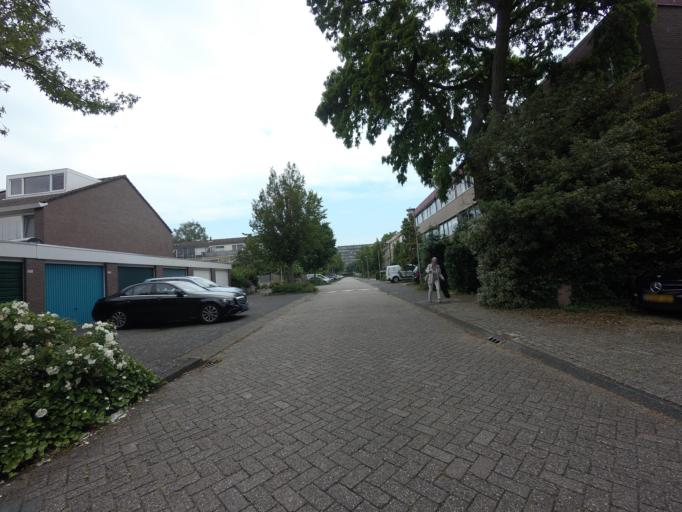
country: NL
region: North Holland
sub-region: Gemeente Purmerend
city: Purmerend
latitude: 52.5221
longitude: 4.9607
